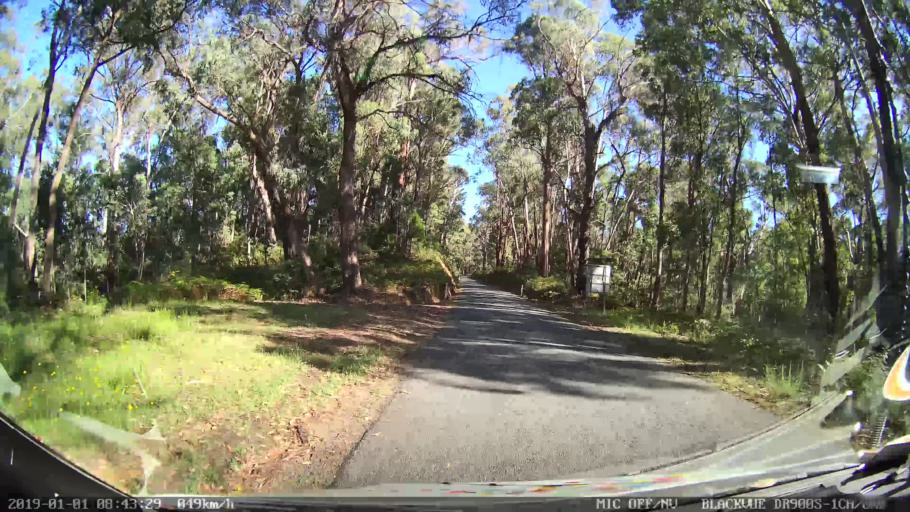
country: AU
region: New South Wales
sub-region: Snowy River
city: Jindabyne
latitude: -36.3169
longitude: 148.1929
